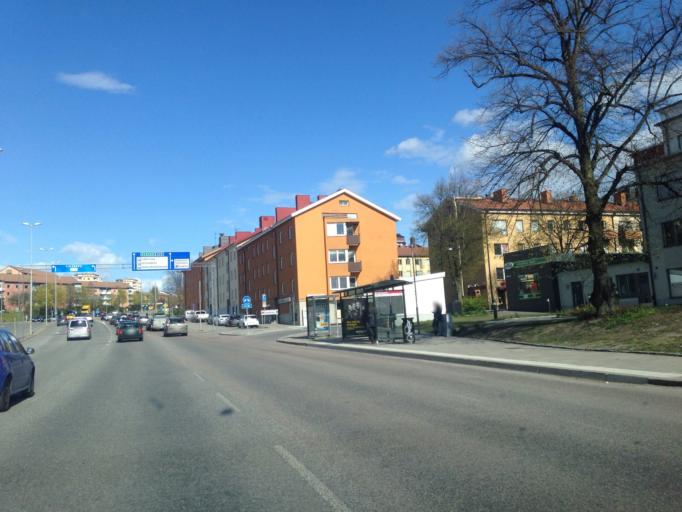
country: SE
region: Stockholm
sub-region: Sodertalje Kommun
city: Soedertaelje
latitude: 59.2003
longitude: 17.6302
